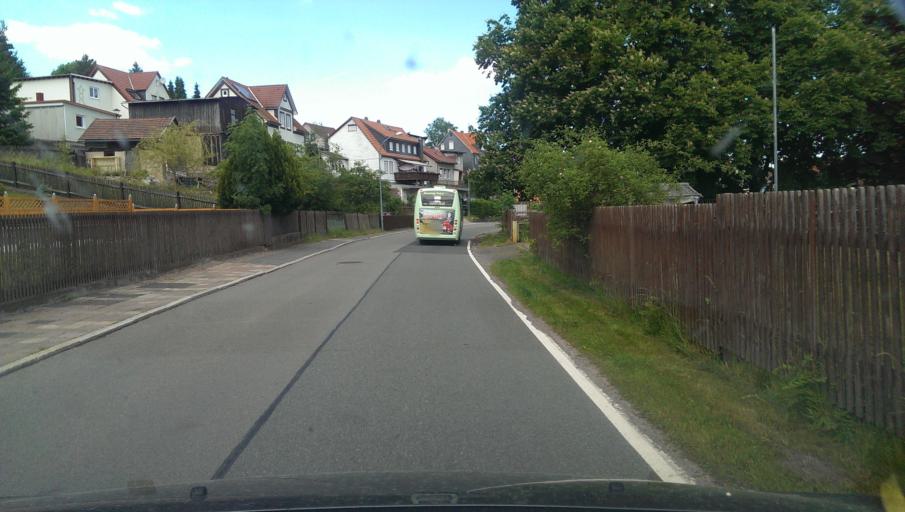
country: DE
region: Thuringia
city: Grafenroda
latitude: 50.7415
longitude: 10.8004
